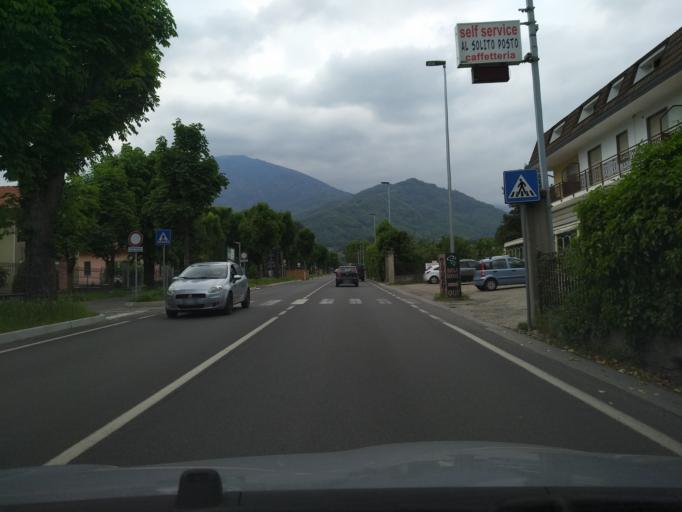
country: IT
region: Piedmont
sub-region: Provincia di Torino
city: Luserna
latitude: 44.8163
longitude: 7.2402
